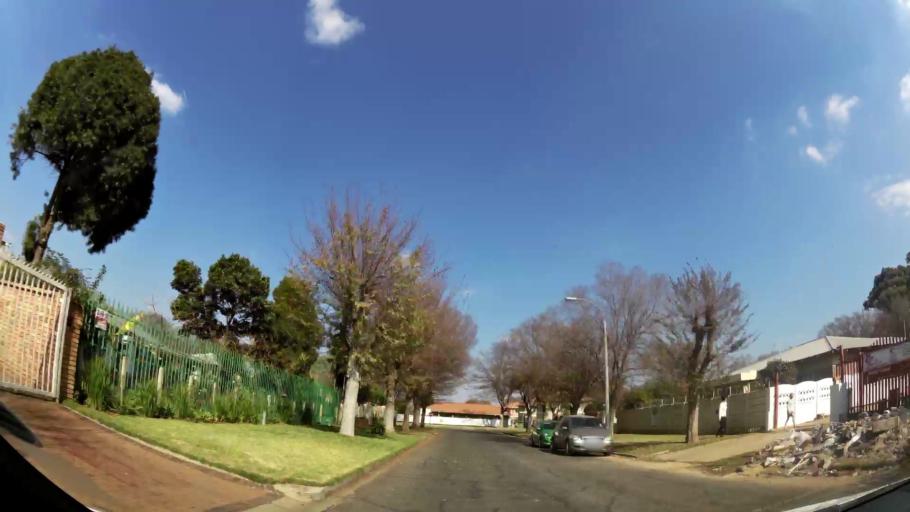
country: ZA
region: Gauteng
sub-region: Ekurhuleni Metropolitan Municipality
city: Boksburg
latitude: -26.2009
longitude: 28.2380
